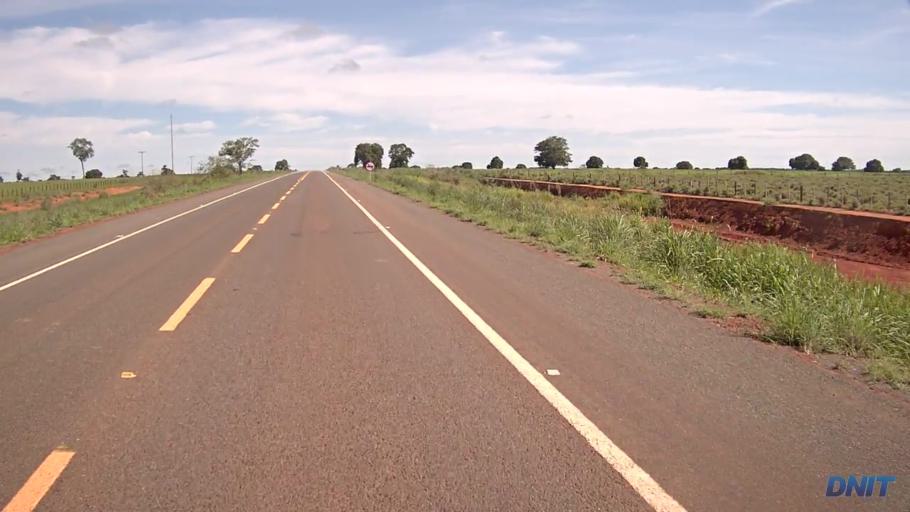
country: BR
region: Goias
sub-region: Sao Miguel Do Araguaia
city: Sao Miguel do Araguaia
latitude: -13.3746
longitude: -50.1426
